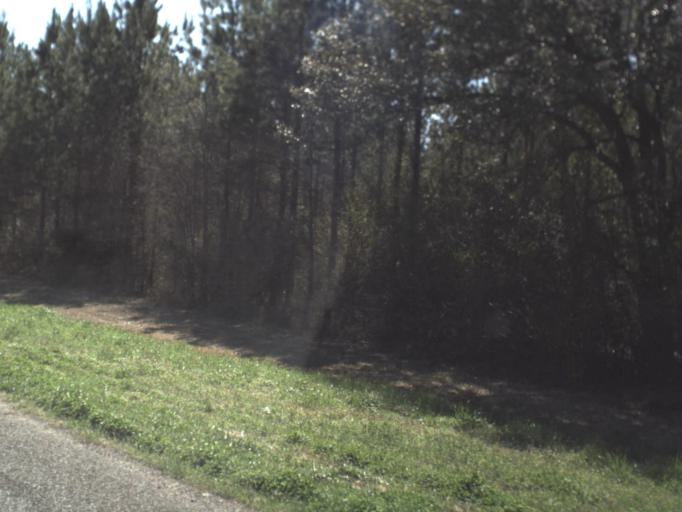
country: US
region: Florida
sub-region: Jackson County
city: Graceville
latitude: 30.9667
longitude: -85.4078
